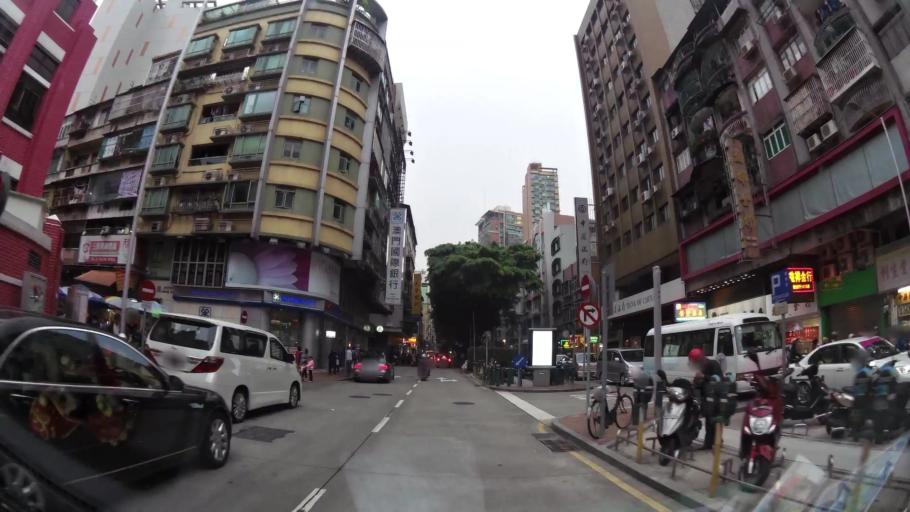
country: MO
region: Macau
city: Macau
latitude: 22.2050
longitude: 113.5444
